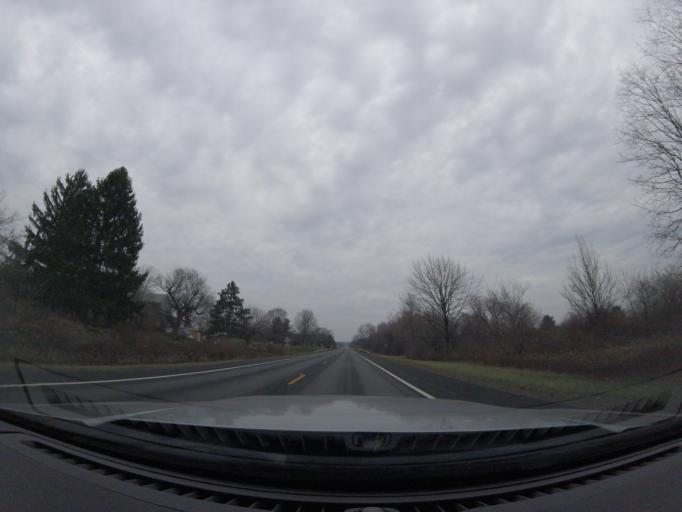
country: US
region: New York
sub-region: Schuyler County
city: Watkins Glen
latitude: 42.4598
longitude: -76.9135
